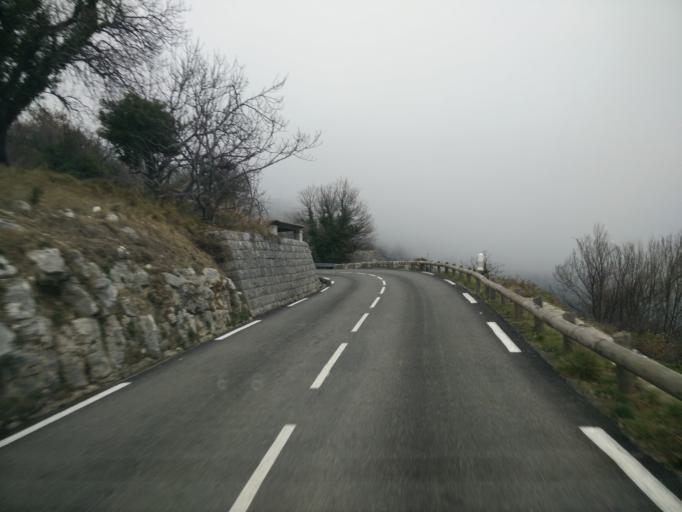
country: FR
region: Provence-Alpes-Cote d'Azur
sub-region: Departement des Alpes-Maritimes
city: Opio
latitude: 43.7199
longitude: 6.9697
